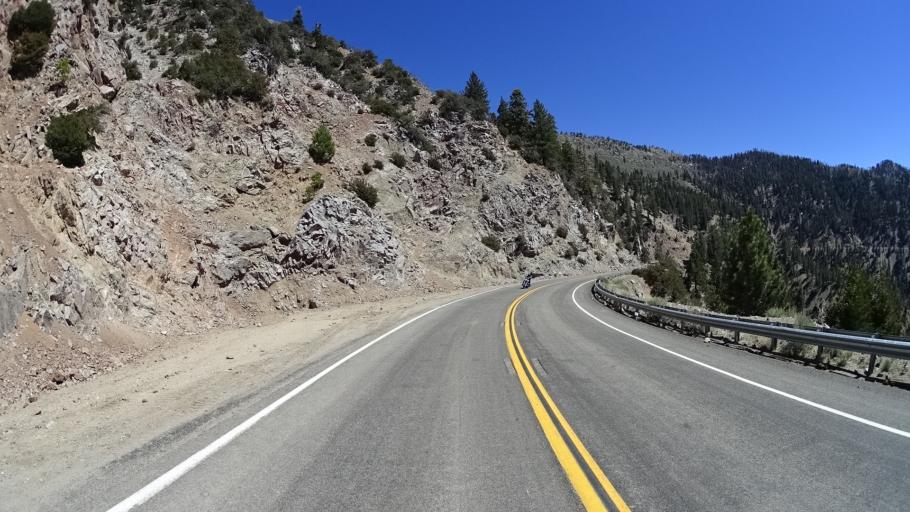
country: US
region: California
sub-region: San Bernardino County
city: Wrightwood
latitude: 34.3565
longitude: -117.8097
